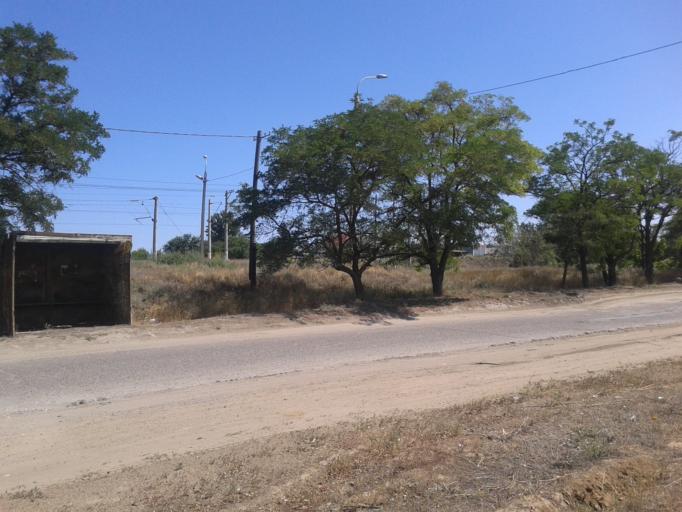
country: RU
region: Volgograd
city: Volgograd
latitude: 48.6889
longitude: 44.4508
